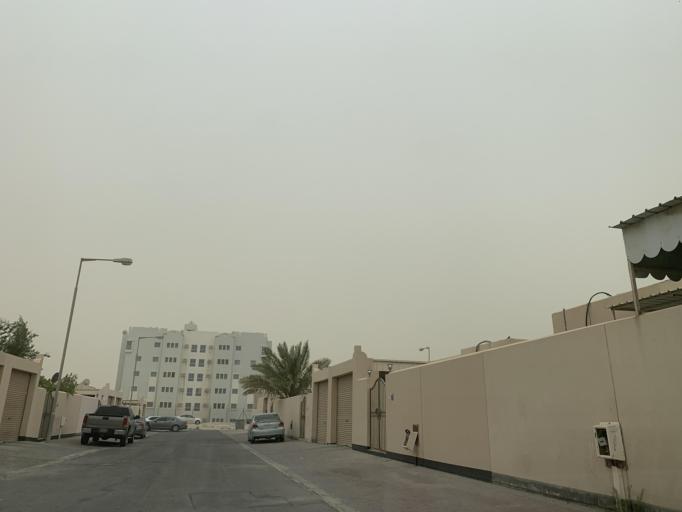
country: BH
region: Central Governorate
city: Madinat Hamad
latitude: 26.1330
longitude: 50.5245
